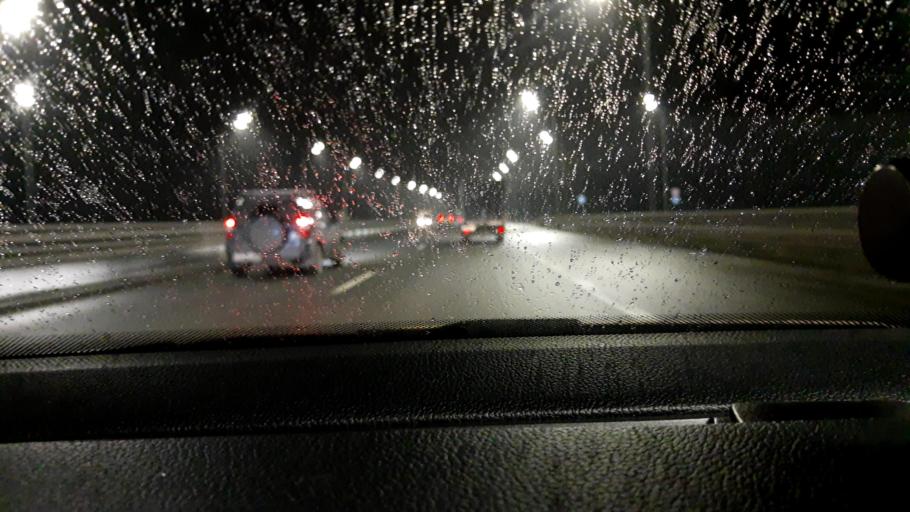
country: RU
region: Moskovskaya
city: Noginsk
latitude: 55.8558
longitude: 38.5483
